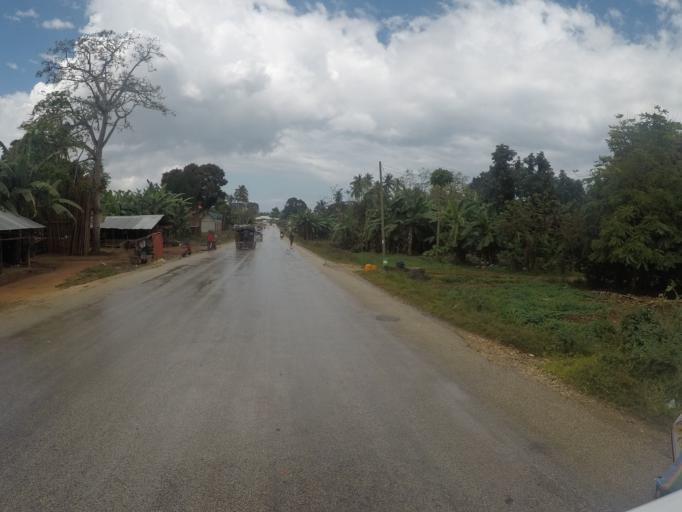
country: TZ
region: Zanzibar Central/South
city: Koani
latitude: -6.0496
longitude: 39.2263
